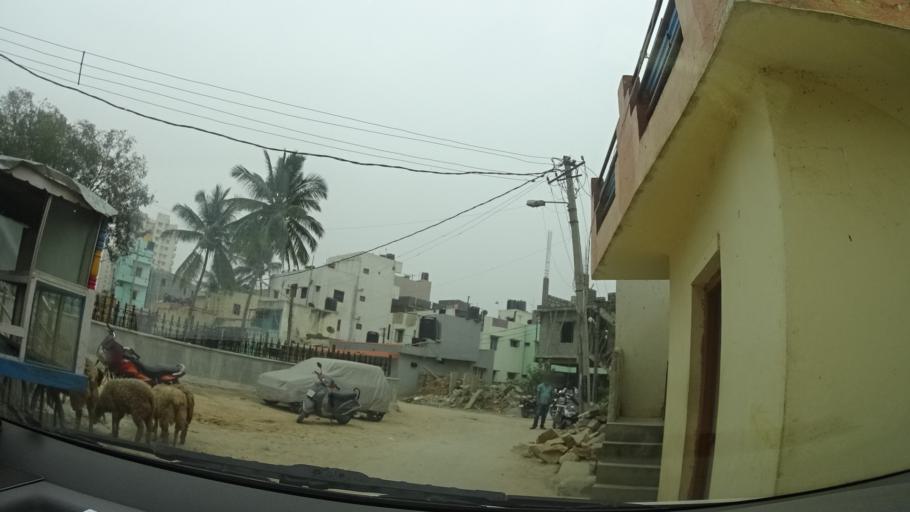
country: IN
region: Karnataka
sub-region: Bangalore Urban
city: Bangalore
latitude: 13.0347
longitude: 77.6339
